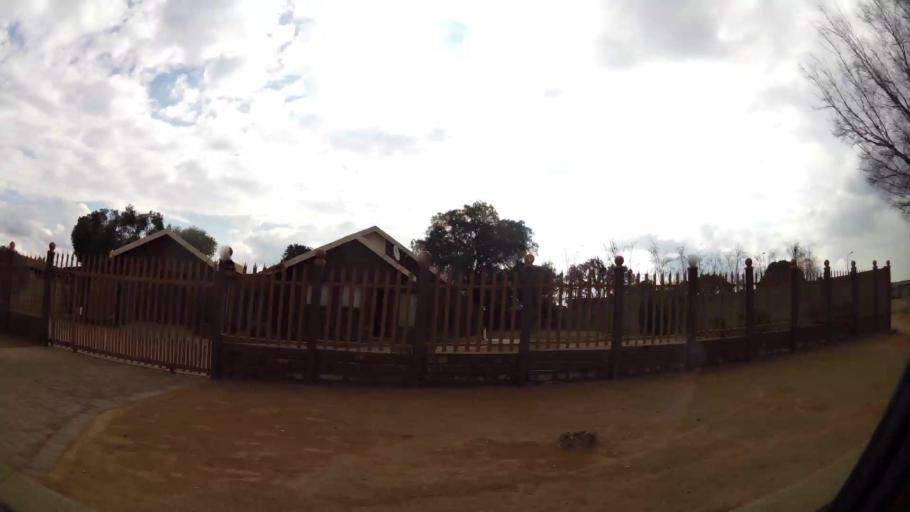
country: ZA
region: Gauteng
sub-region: Sedibeng District Municipality
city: Vanderbijlpark
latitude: -26.7037
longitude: 27.8048
